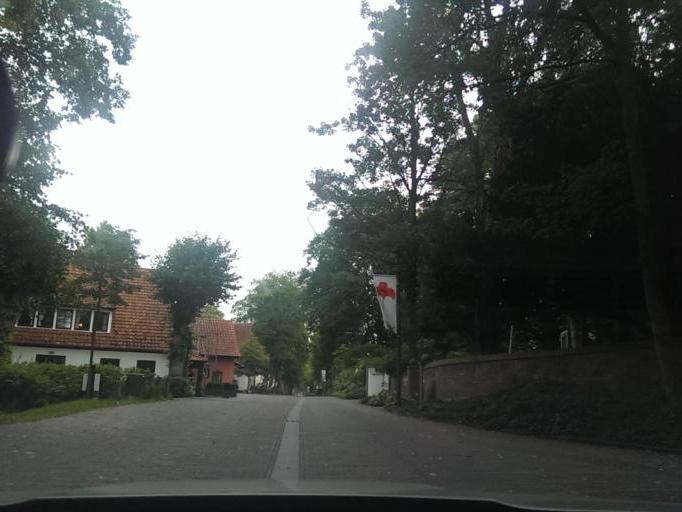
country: DE
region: Lower Saxony
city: Worpswede
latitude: 53.2214
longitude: 8.9225
